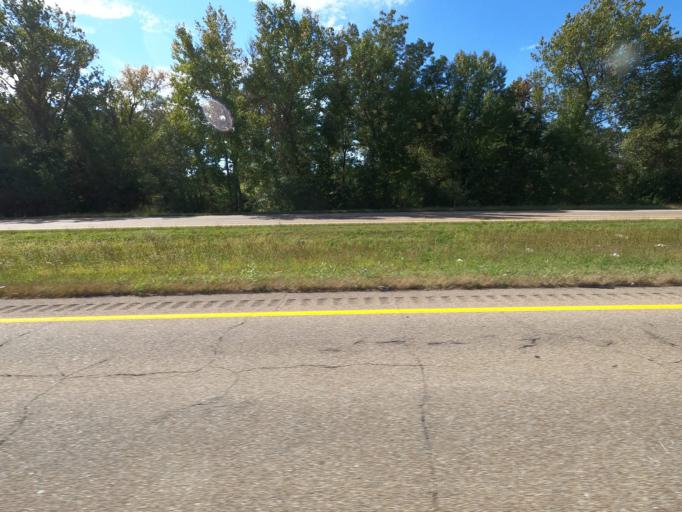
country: US
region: Tennessee
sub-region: Crockett County
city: Alamo
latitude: 35.8740
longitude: -89.2187
